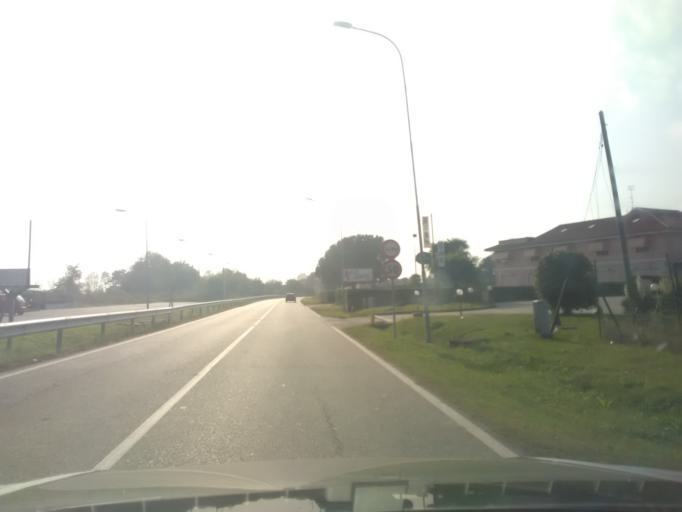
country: IT
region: Piedmont
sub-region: Provincia di Vercelli
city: Alice Castello
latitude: 45.3626
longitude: 8.0796
